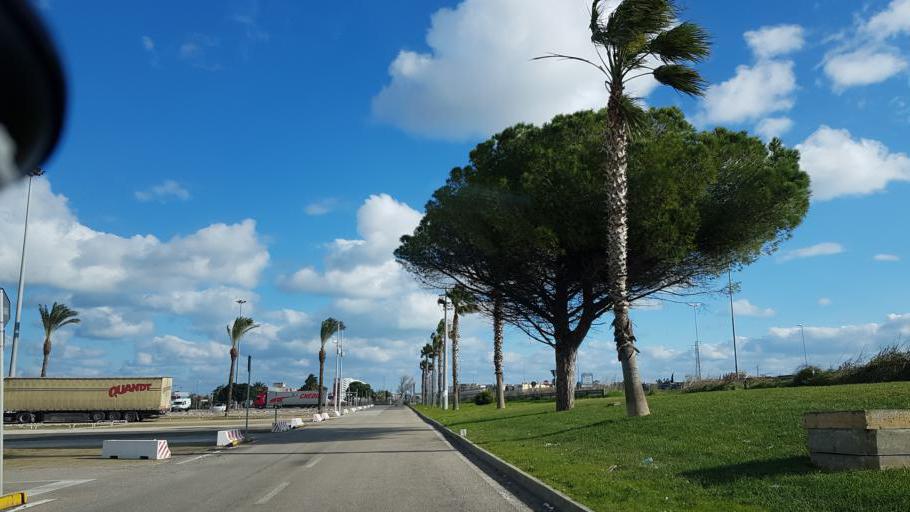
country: IT
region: Apulia
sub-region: Provincia di Brindisi
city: Brindisi
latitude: 40.6167
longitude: 17.9030
